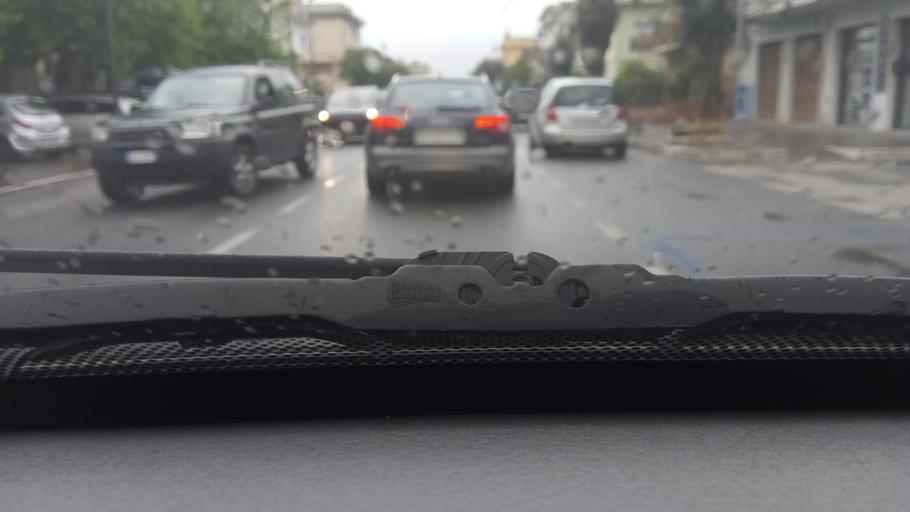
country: IT
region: Latium
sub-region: Provincia di Latina
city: Penitro
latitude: 41.2565
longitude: 13.7080
